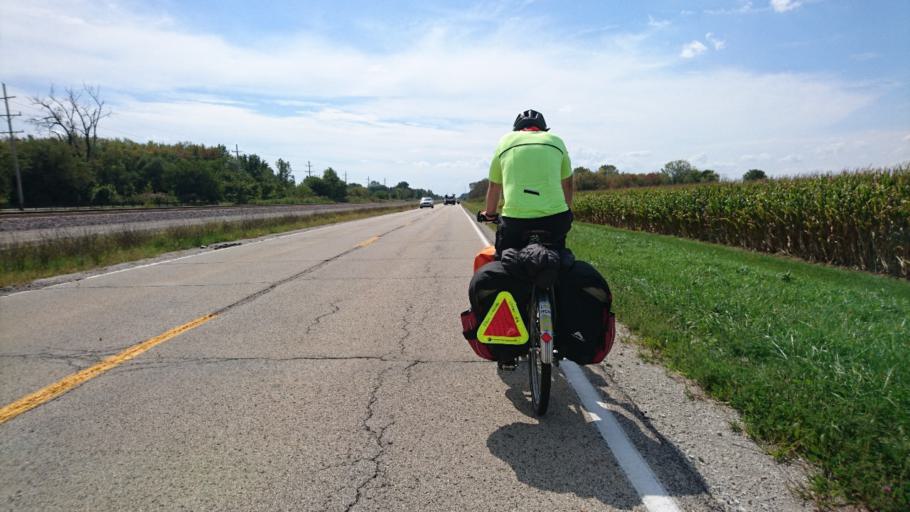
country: US
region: Illinois
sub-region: Grundy County
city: Central City
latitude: 41.2364
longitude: -88.2475
